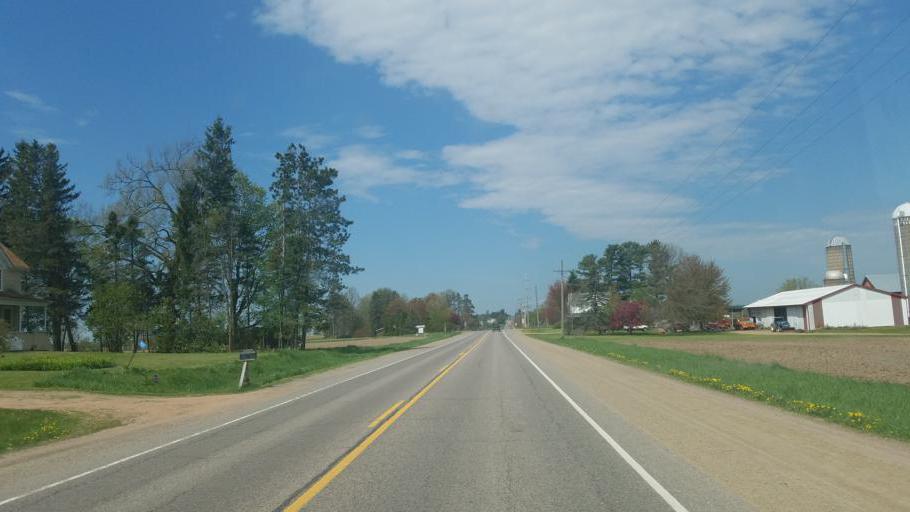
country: US
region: Wisconsin
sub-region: Clark County
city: Loyal
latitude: 44.5826
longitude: -90.3931
